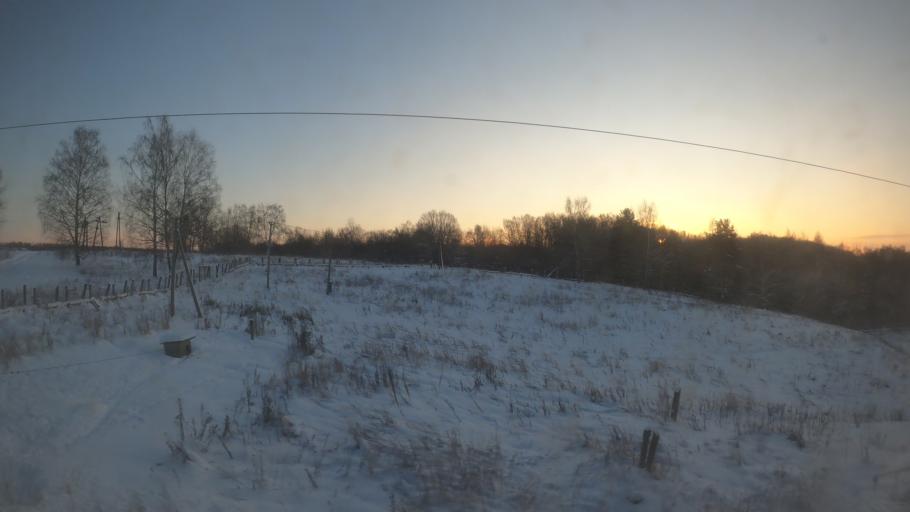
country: RU
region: Moskovskaya
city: Dedenevo
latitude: 56.2617
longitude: 37.5115
